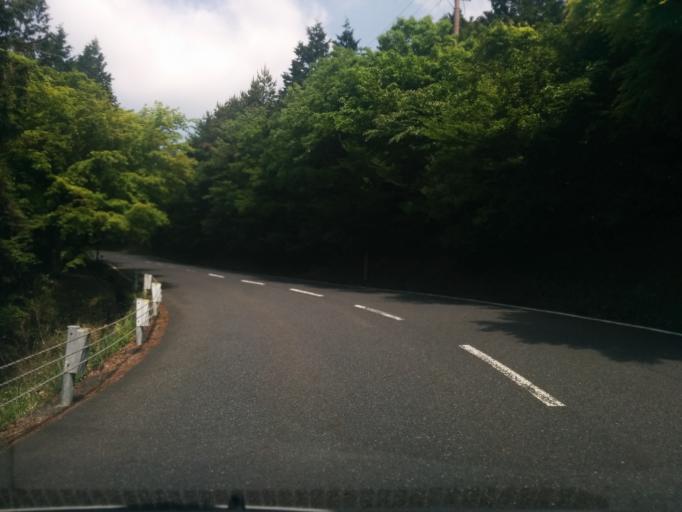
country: JP
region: Shiga Prefecture
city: Otsu-shi
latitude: 35.0528
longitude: 135.8341
